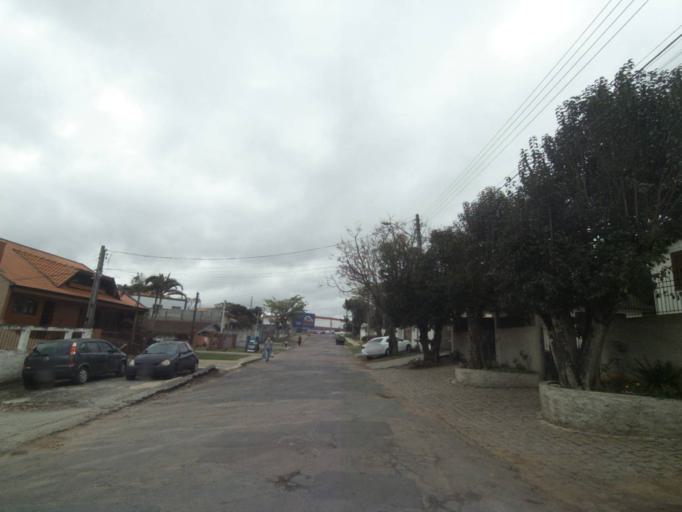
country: BR
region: Parana
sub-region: Sao Jose Dos Pinhais
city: Sao Jose dos Pinhais
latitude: -25.5406
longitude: -49.2953
